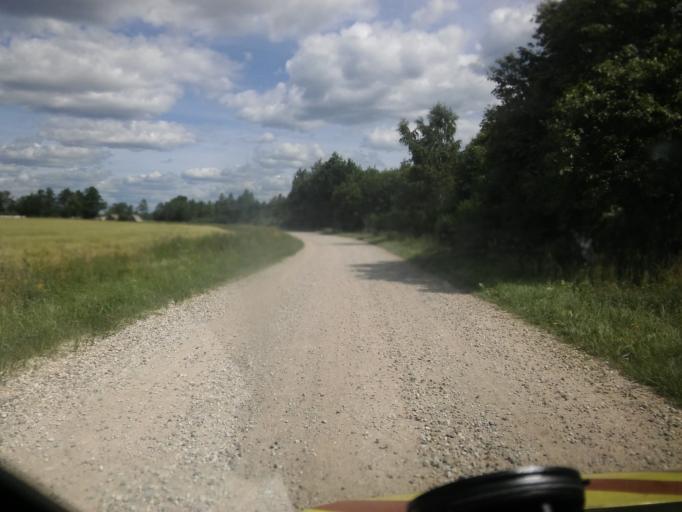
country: LV
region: Aloja
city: Staicele
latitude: 58.0377
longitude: 24.7468
